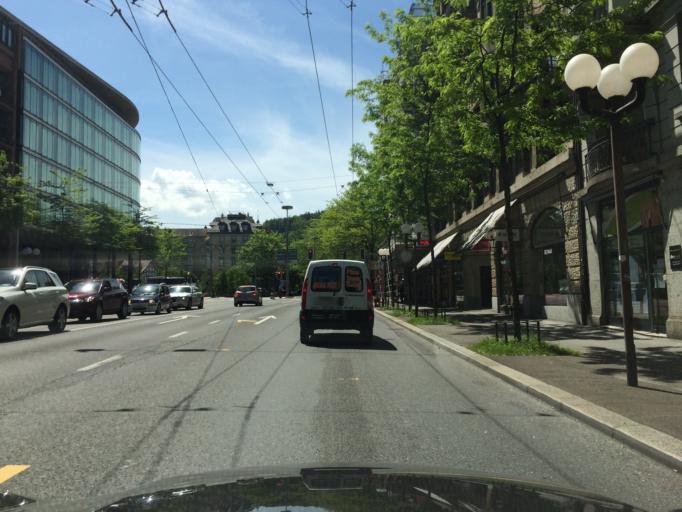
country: CH
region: Lucerne
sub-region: Lucerne-Stadt District
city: Luzern
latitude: 47.0483
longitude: 8.3049
